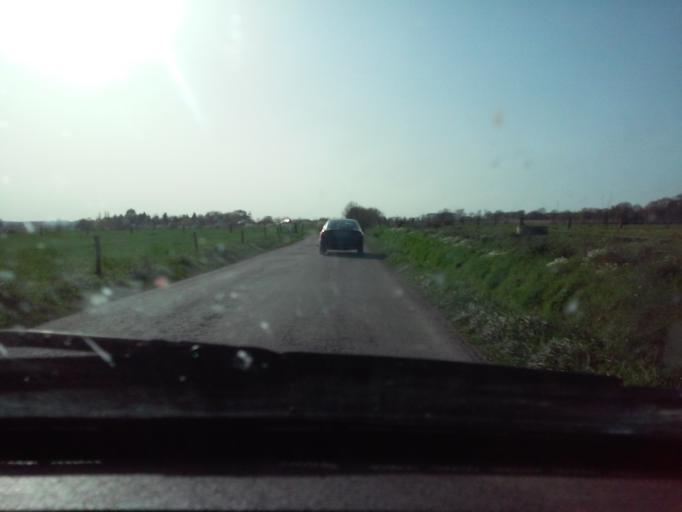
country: FR
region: Brittany
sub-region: Departement d'Ille-et-Vilaine
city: Saint-Sauveur-des-Landes
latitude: 48.3005
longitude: -1.3246
